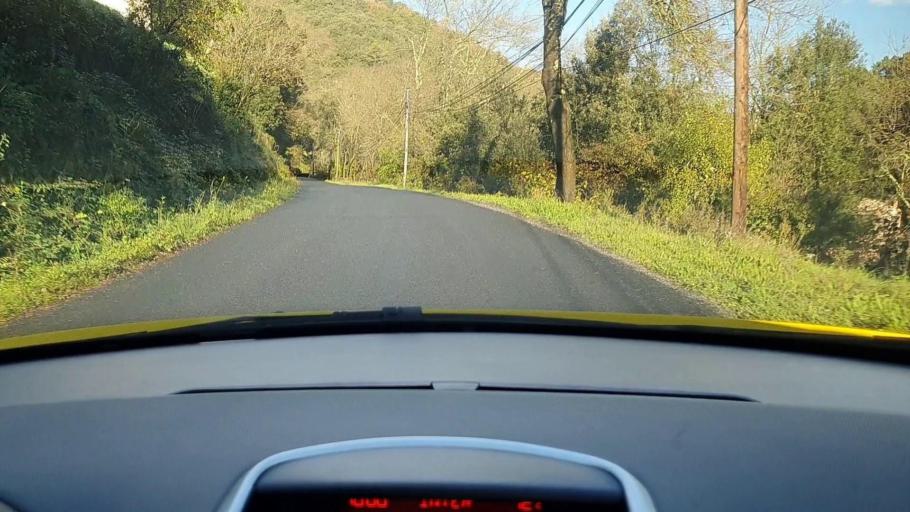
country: FR
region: Languedoc-Roussillon
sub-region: Departement du Gard
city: Sumene
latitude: 43.9879
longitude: 3.7142
